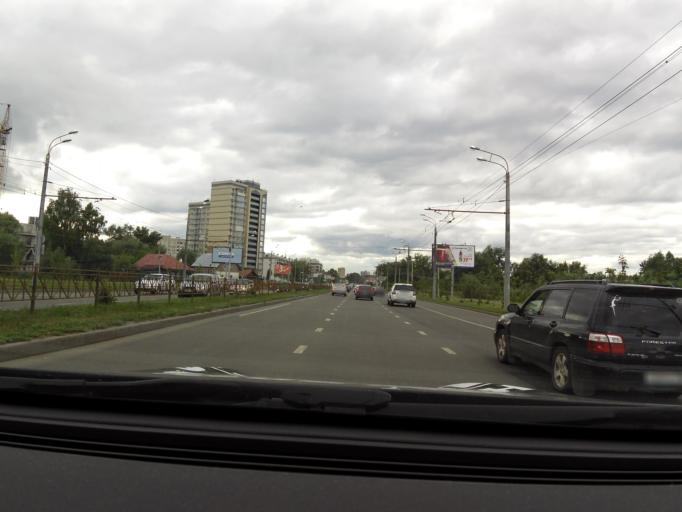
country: RU
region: Tatarstan
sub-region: Gorod Kazan'
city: Kazan
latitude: 55.8132
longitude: 49.0745
